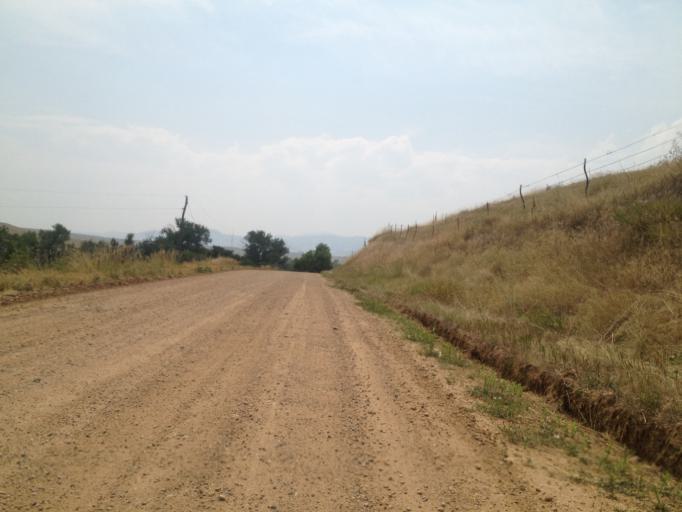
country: US
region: Colorado
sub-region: Boulder County
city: Superior
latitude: 39.9426
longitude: -105.1907
